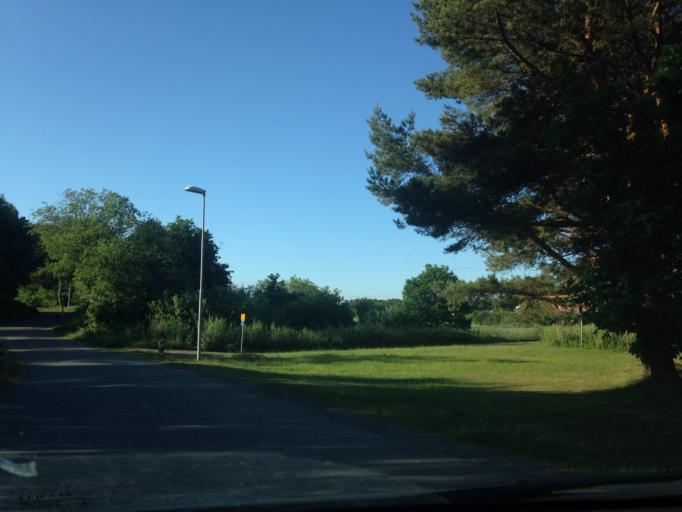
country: SE
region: Vaestra Goetaland
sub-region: Goteborg
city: Torslanda
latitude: 57.7683
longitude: 11.8380
